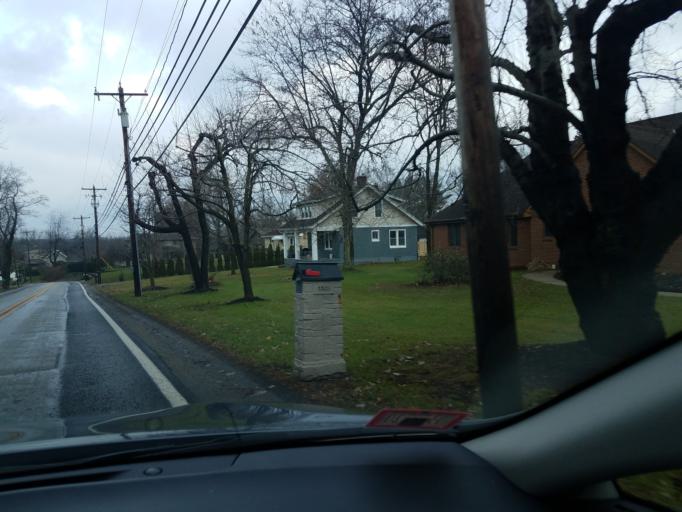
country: US
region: Pennsylvania
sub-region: Allegheny County
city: Franklin Park
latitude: 40.5809
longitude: -80.0805
